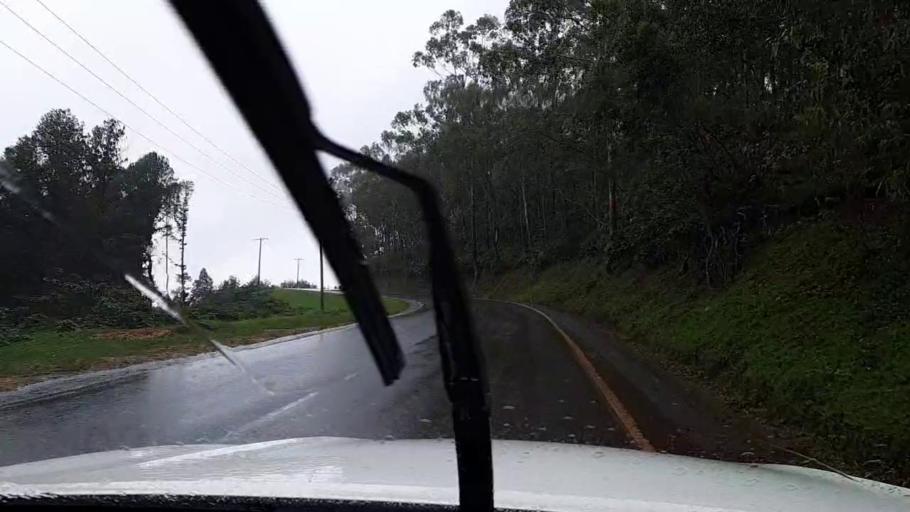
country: RW
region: Western Province
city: Cyangugu
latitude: -2.4624
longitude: 28.9944
